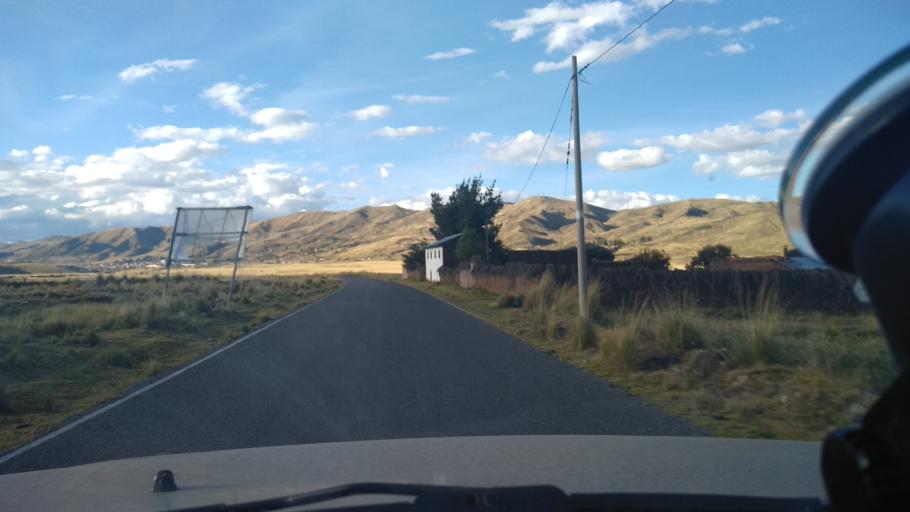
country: PE
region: Cusco
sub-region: Provincia de Canas
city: Chignayhua
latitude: -14.2495
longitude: -71.4357
